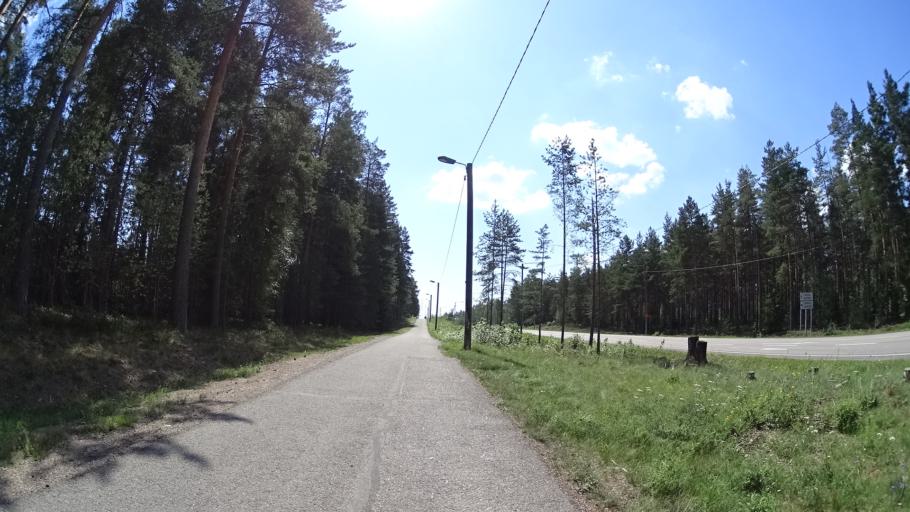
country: FI
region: Uusimaa
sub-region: Helsinki
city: Vantaa
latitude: 60.3181
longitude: 25.0004
